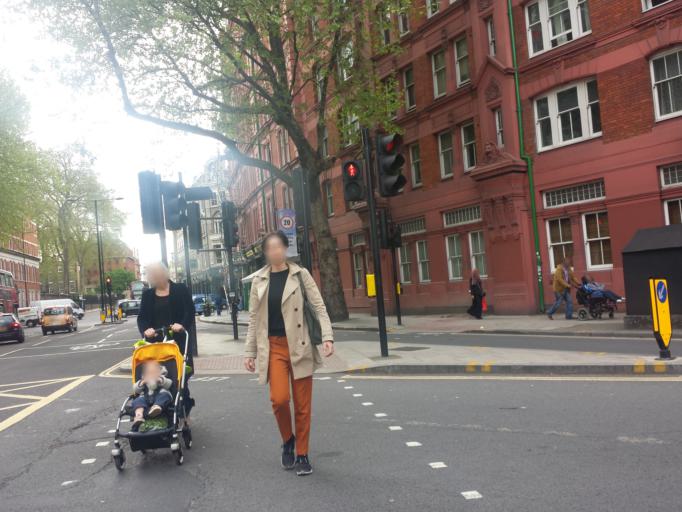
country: GB
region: England
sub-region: Greater London
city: Clerkenwell
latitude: 51.5216
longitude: -0.1123
